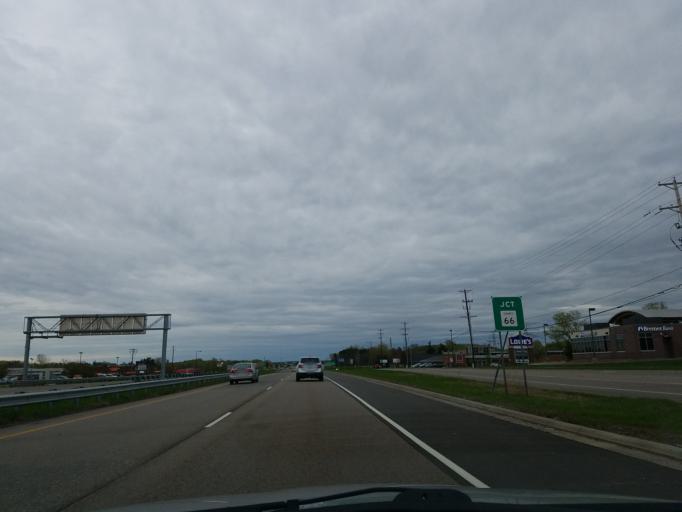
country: US
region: Minnesota
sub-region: Washington County
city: Stillwater
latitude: 45.0360
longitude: -92.8287
